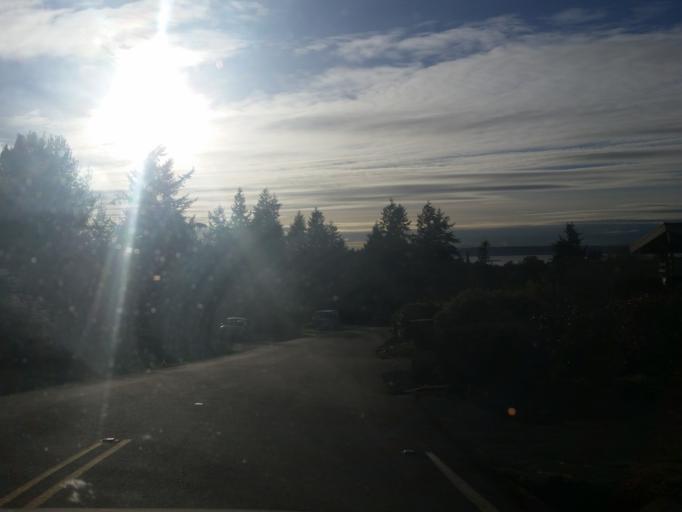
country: US
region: Washington
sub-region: King County
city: Shoreline
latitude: 47.7134
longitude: -122.3638
